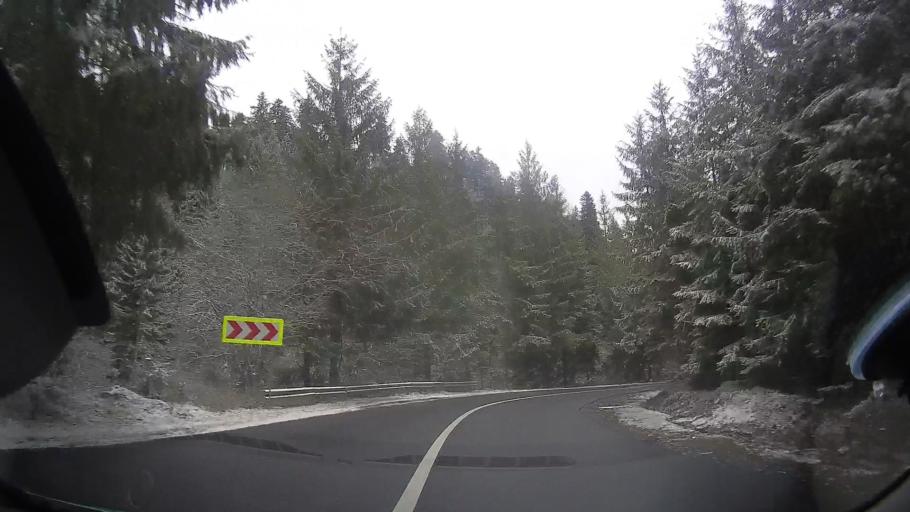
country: RO
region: Cluj
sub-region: Comuna Calatele
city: Calatele
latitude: 46.7342
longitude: 23.0389
